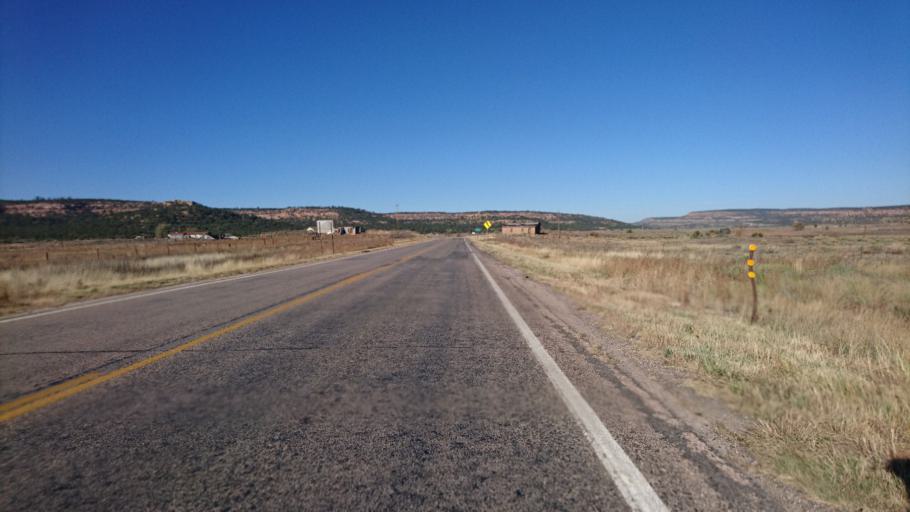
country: US
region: New Mexico
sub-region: McKinley County
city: Black Rock
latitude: 35.1061
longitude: -108.5789
